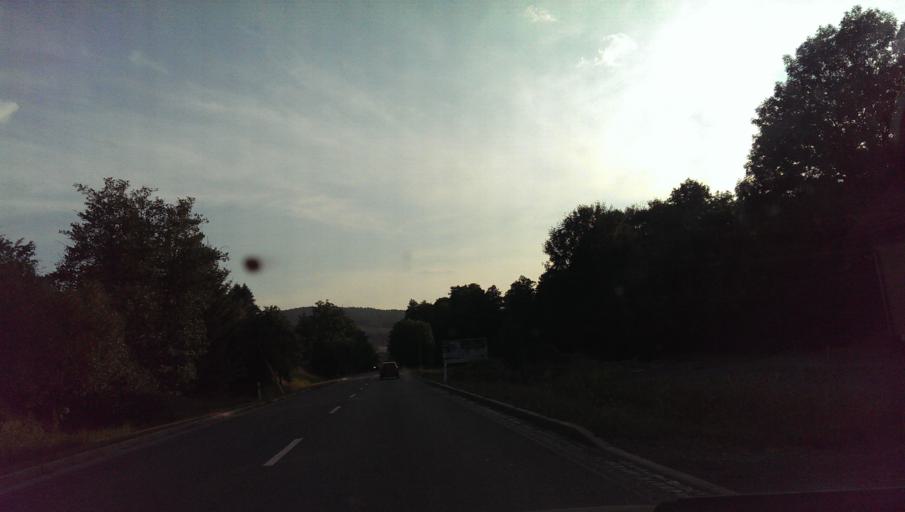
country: CZ
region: Zlin
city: Pozlovice
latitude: 49.1342
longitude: 17.8086
